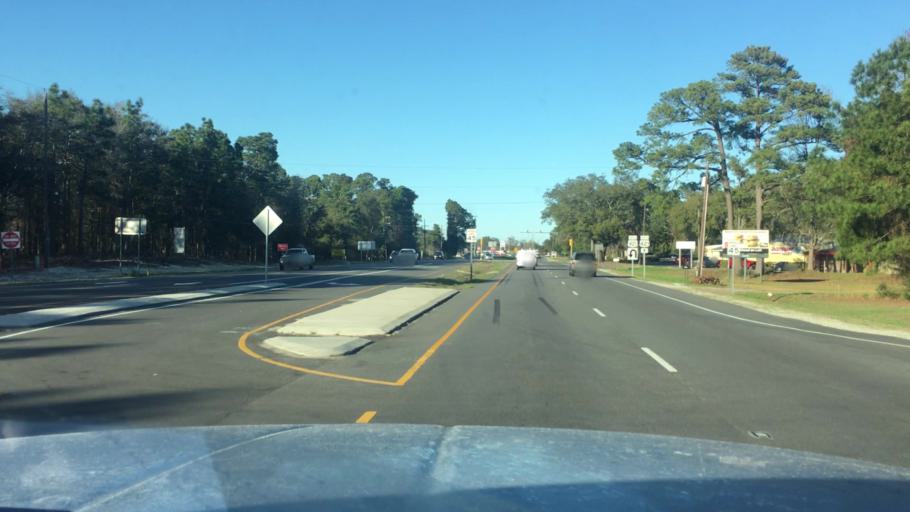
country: US
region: North Carolina
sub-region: New Hanover County
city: Myrtle Grove
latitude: 34.1298
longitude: -77.8972
